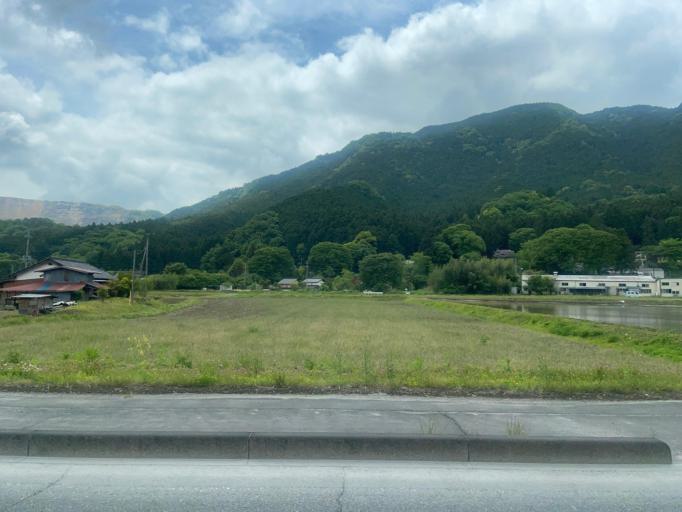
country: JP
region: Tochigi
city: Tanuma
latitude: 36.4629
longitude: 139.6379
